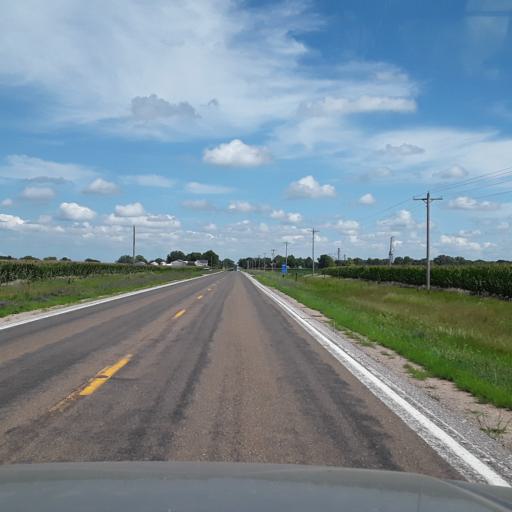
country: US
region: Nebraska
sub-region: Polk County
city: Stromsburg
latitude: 41.0159
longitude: -97.4062
